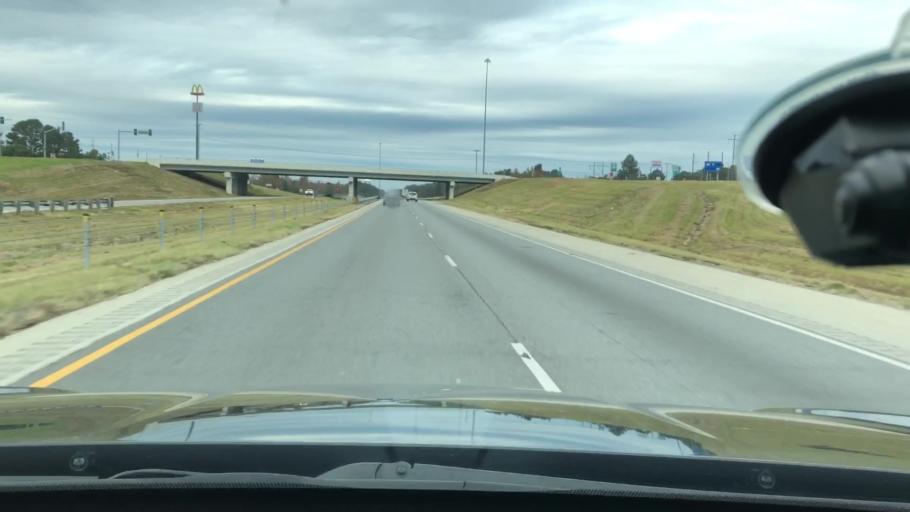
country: US
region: Arkansas
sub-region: Clark County
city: Arkadelphia
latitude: 34.1166
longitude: -93.0939
